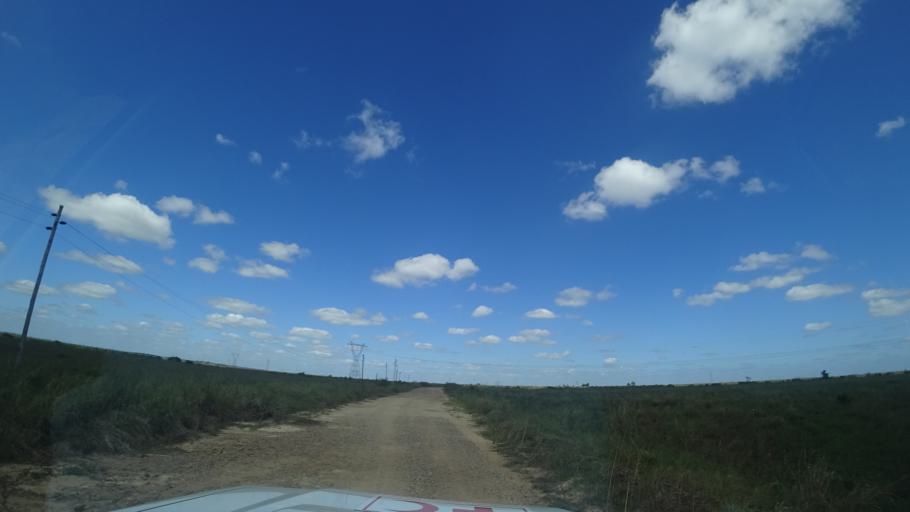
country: MZ
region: Sofala
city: Dondo
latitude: -19.4578
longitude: 34.5630
